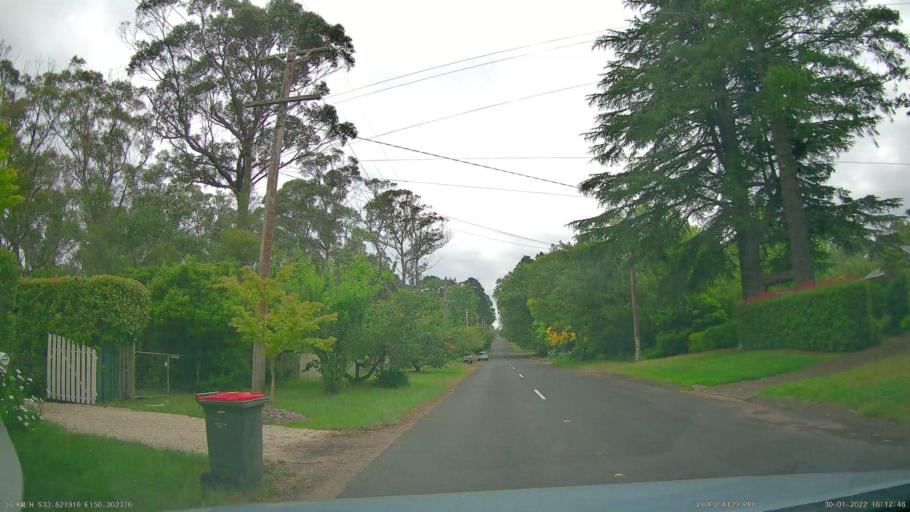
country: AU
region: New South Wales
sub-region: Blue Mountains Municipality
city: Blackheath
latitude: -33.6220
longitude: 150.3023
